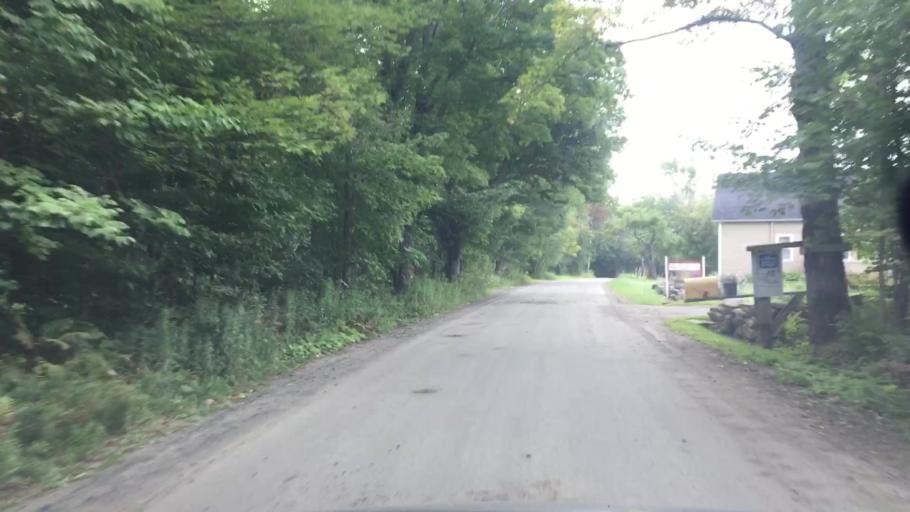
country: US
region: Vermont
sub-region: Windham County
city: Dover
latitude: 42.8278
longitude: -72.7974
